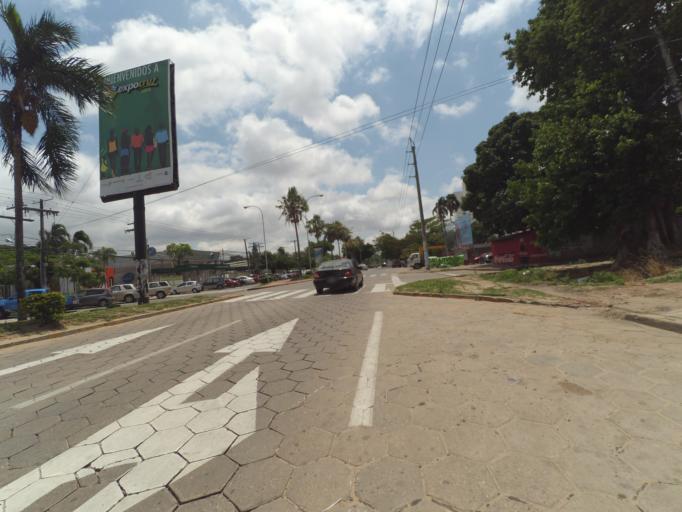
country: BO
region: Santa Cruz
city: Santa Cruz de la Sierra
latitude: -17.7856
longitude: -63.2082
